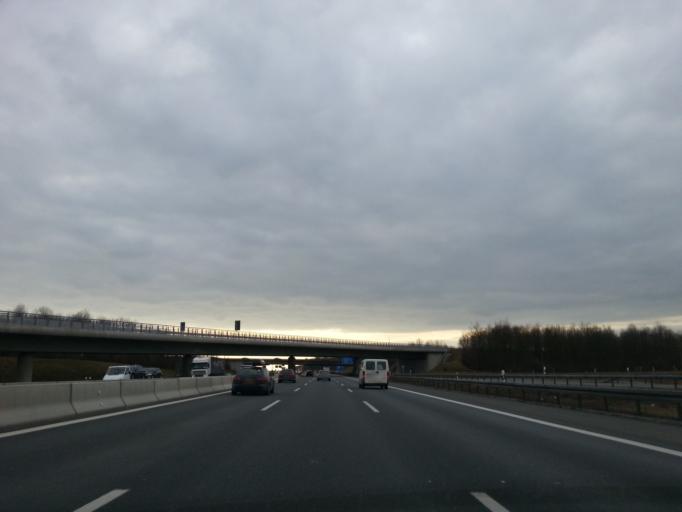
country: DE
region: Bavaria
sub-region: Regierungsbezirk Unterfranken
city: Biebelried
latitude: 49.7804
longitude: 10.0963
